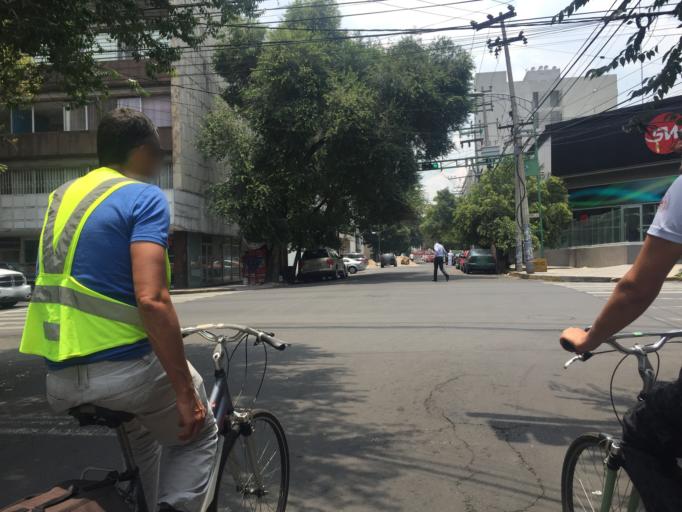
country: MX
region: Mexico City
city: Benito Juarez
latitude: 19.4160
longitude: -99.1635
